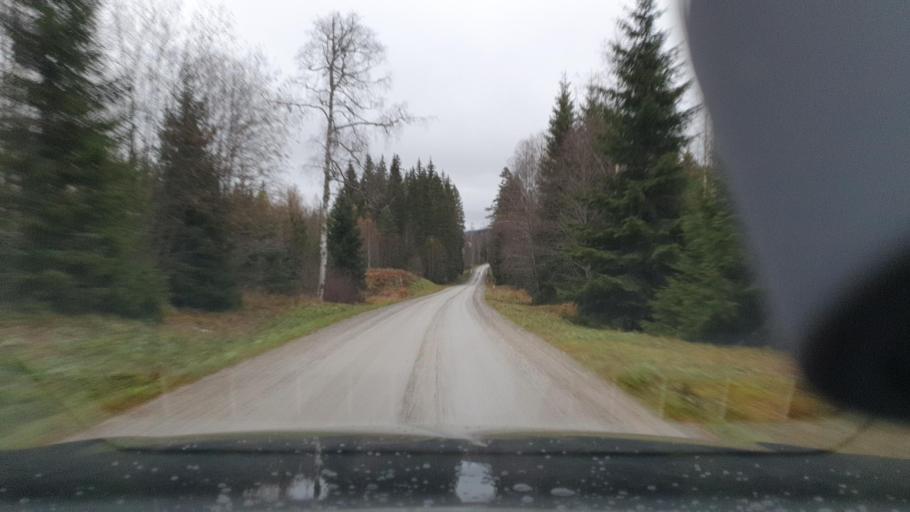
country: SE
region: Vaermland
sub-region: Arvika Kommun
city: Arvika
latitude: 59.8202
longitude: 12.7433
